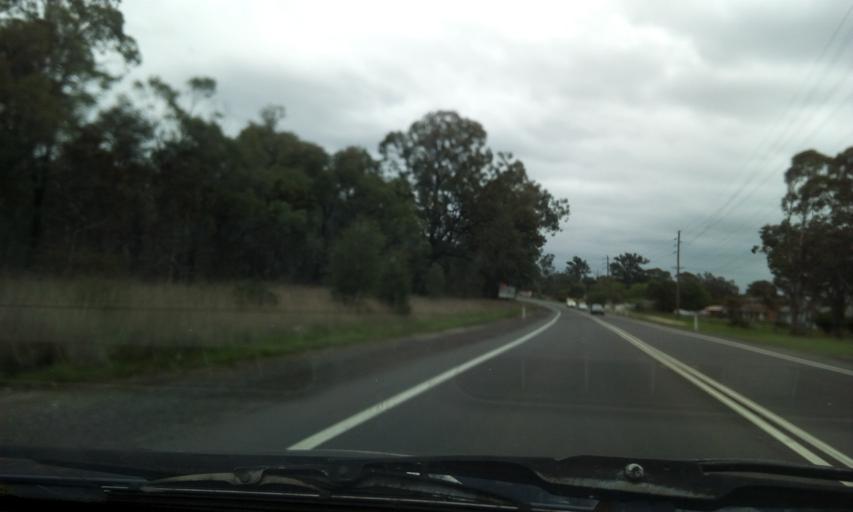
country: AU
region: New South Wales
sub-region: Hawkesbury
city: South Windsor
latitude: -33.6585
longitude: 150.7662
